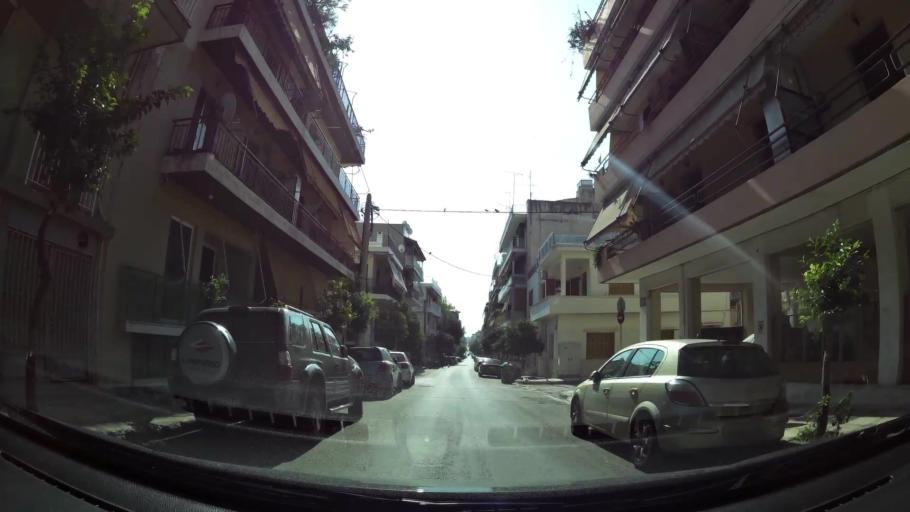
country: GR
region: Attica
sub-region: Nomos Piraios
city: Keratsini
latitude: 37.9608
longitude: 23.6311
